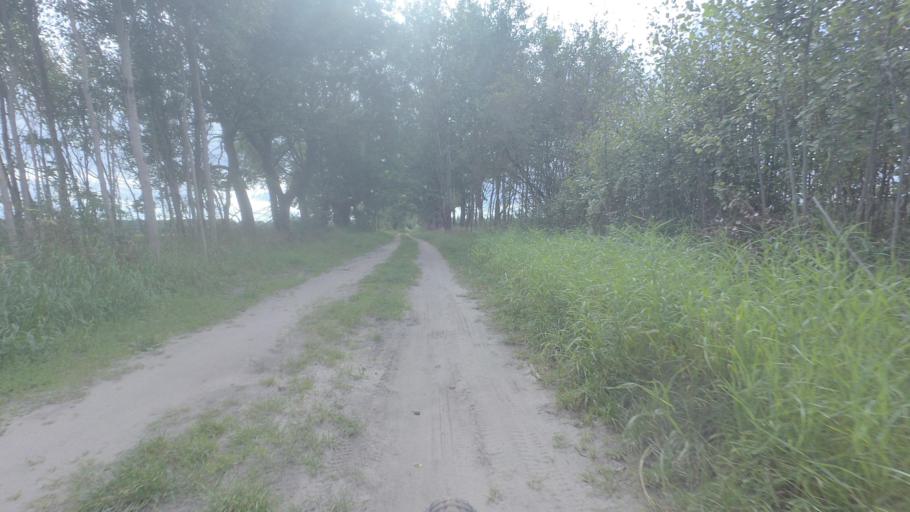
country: DE
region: Brandenburg
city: Ludwigsfelde
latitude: 52.3247
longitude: 13.2084
